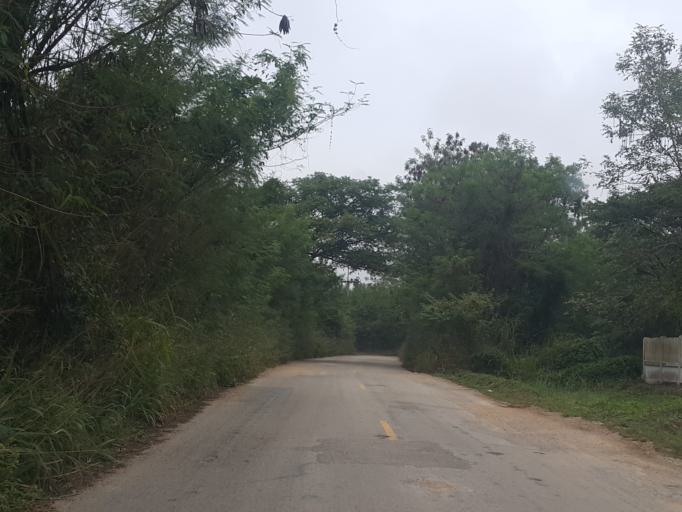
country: TH
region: Lampang
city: Lampang
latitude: 18.3335
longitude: 99.4861
